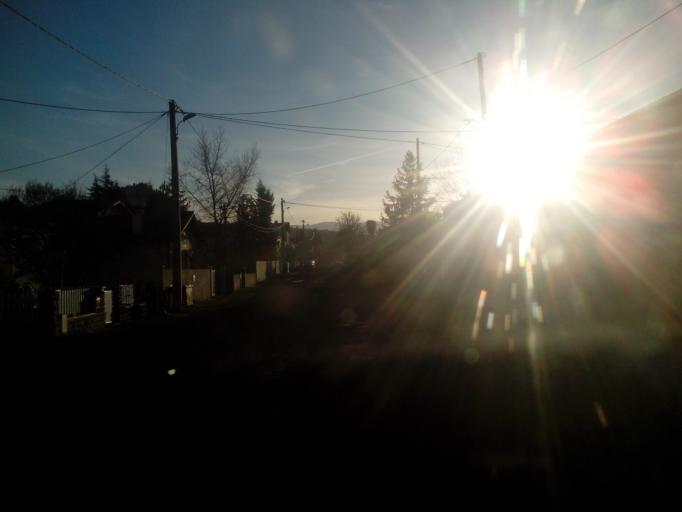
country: FR
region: Languedoc-Roussillon
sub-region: Departement de l'Aude
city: Esperaza
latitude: 42.9395
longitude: 2.2337
